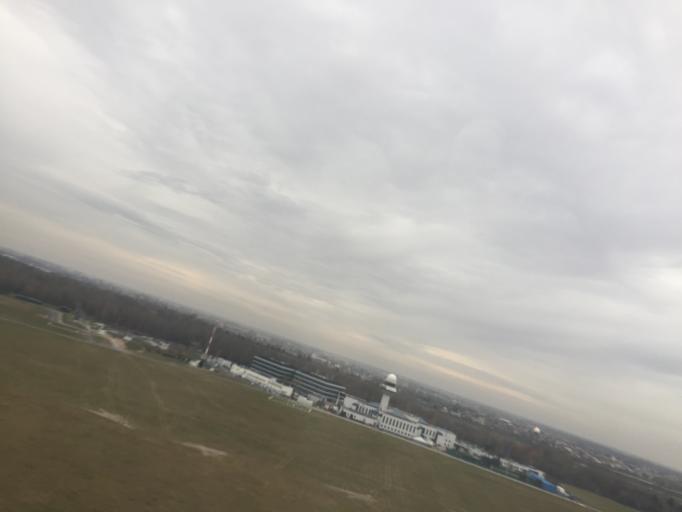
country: PL
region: Masovian Voivodeship
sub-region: Warszawa
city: Wlochy
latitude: 52.1668
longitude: 20.9634
